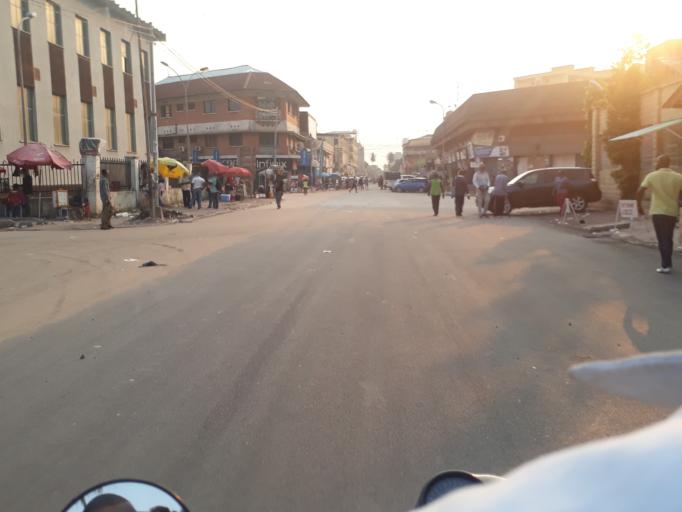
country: CD
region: Kinshasa
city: Kinshasa
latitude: -4.3043
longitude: 15.3143
